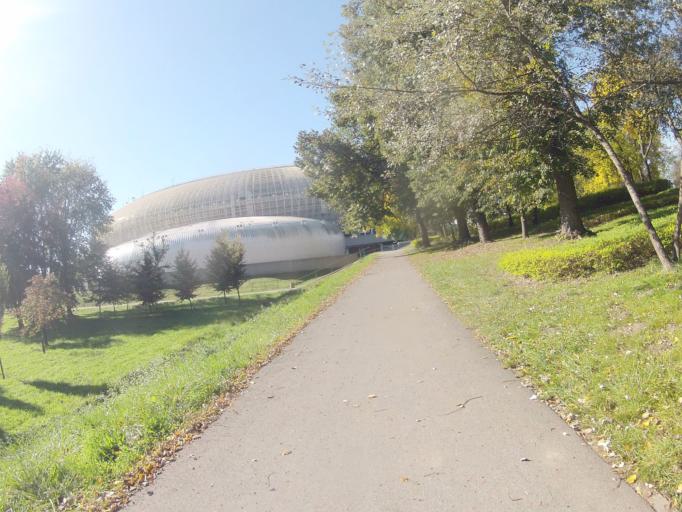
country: PL
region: Lesser Poland Voivodeship
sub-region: Krakow
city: Krakow
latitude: 50.0694
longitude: 19.9932
